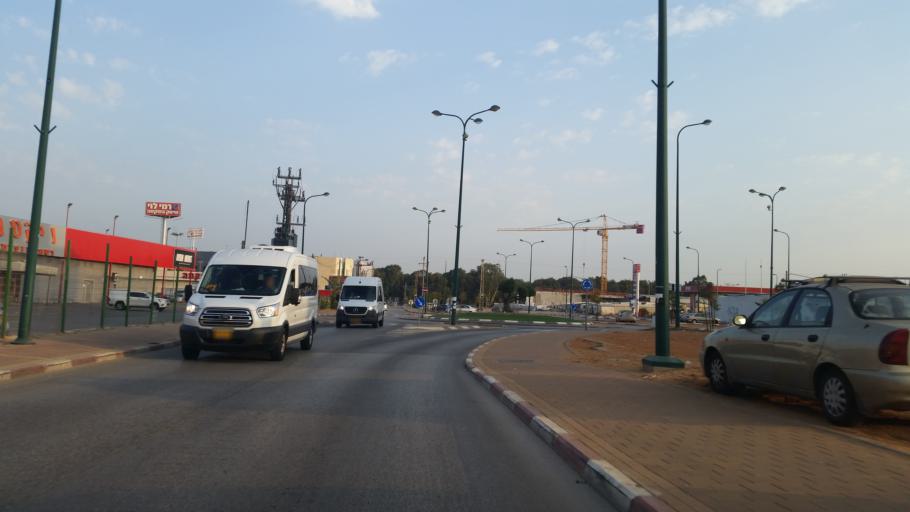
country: IL
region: Central District
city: Netanya
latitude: 32.3200
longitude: 34.8718
